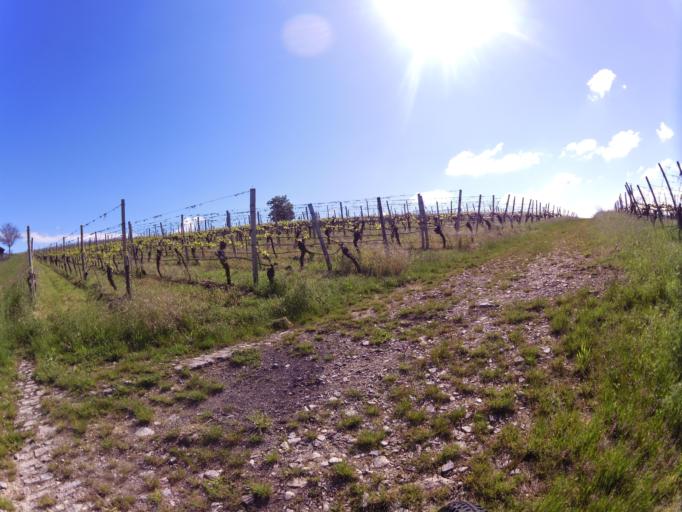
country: DE
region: Bavaria
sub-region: Regierungsbezirk Unterfranken
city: Sommerach
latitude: 49.8373
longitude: 10.1881
